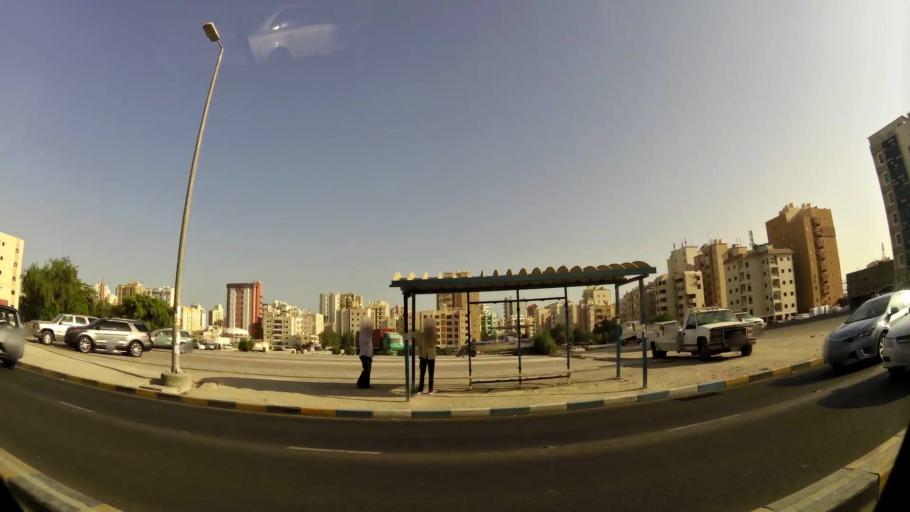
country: KW
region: Muhafazat Hawalli
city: As Salimiyah
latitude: 29.3338
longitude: 48.0833
